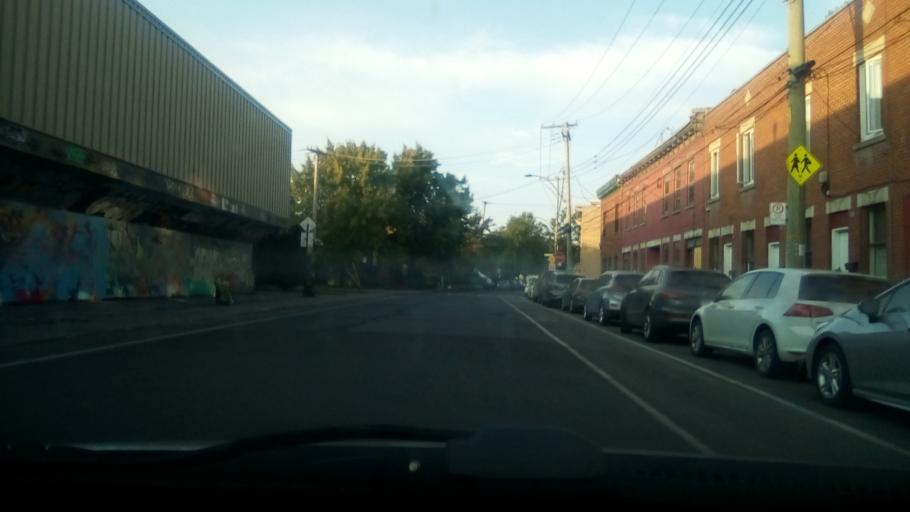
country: CA
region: Quebec
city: Westmount
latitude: 45.4802
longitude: -73.5634
